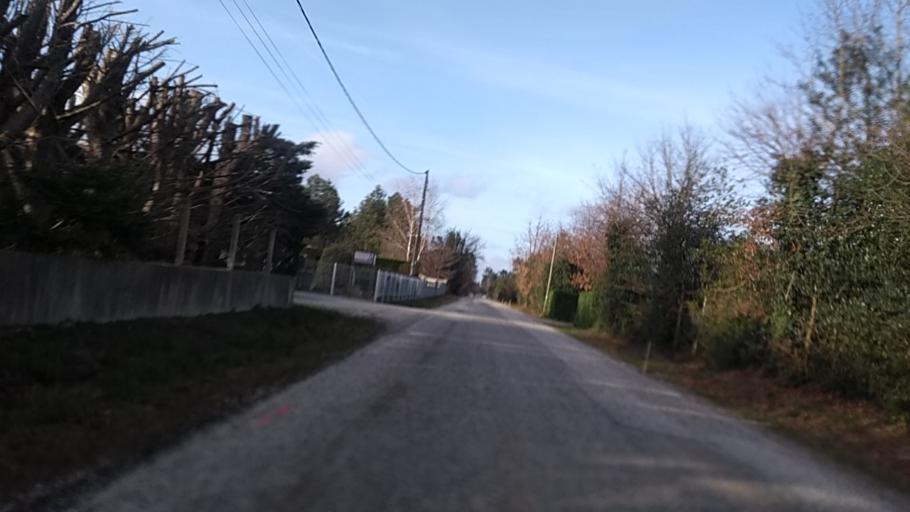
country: FR
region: Aquitaine
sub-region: Departement de la Gironde
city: Le Barp
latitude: 44.5851
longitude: -0.7698
